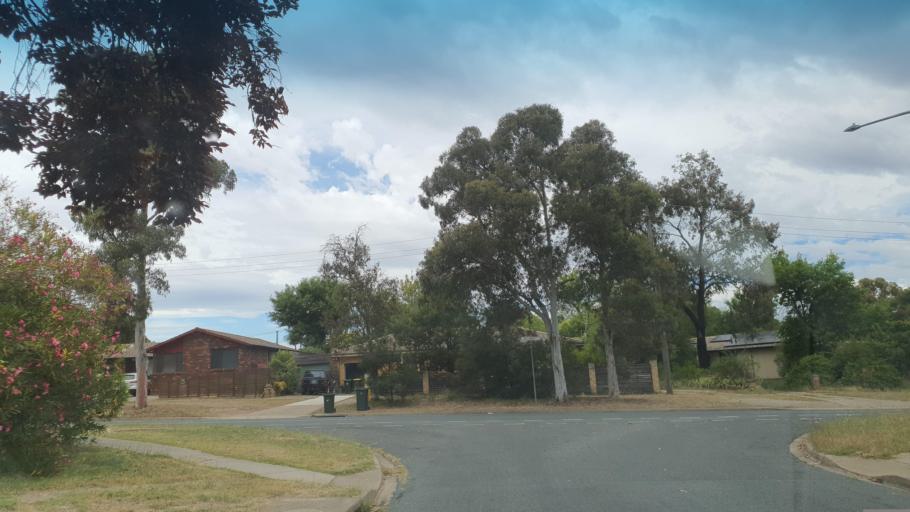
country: AU
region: Australian Capital Territory
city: Belconnen
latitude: -35.2026
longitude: 149.0403
